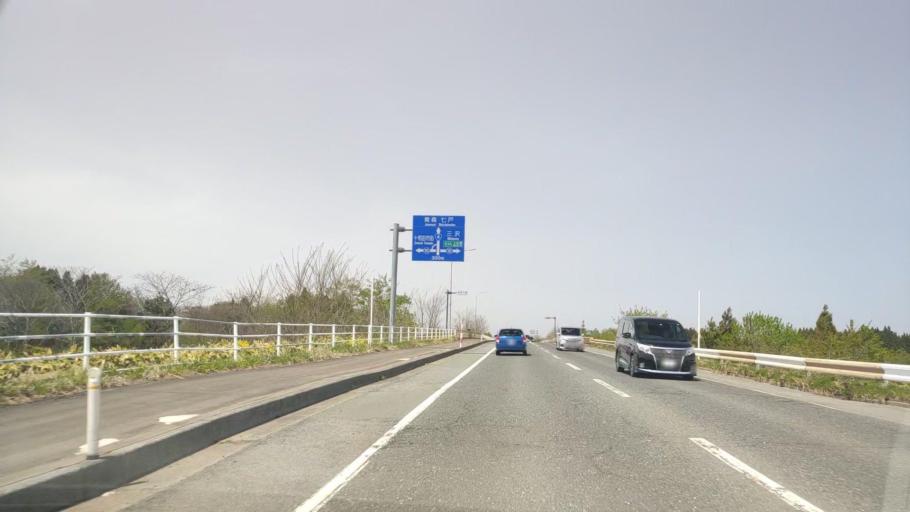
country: JP
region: Aomori
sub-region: Misawa Shi
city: Inuotose
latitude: 40.6305
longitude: 141.2487
